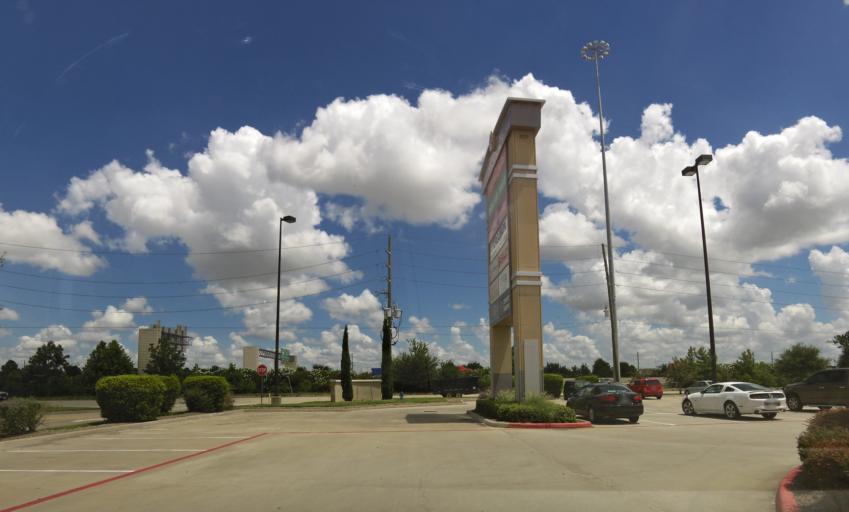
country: US
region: Texas
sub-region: Harris County
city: Katy
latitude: 29.7846
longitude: -95.7950
